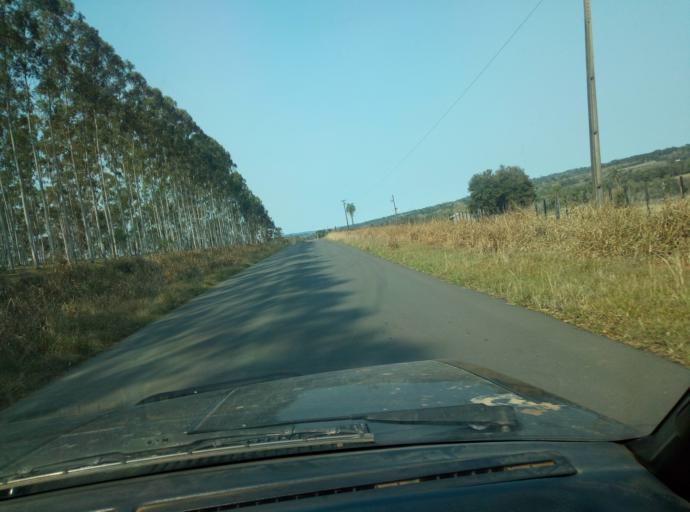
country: PY
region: Caaguazu
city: Carayao
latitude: -25.2548
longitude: -56.2880
